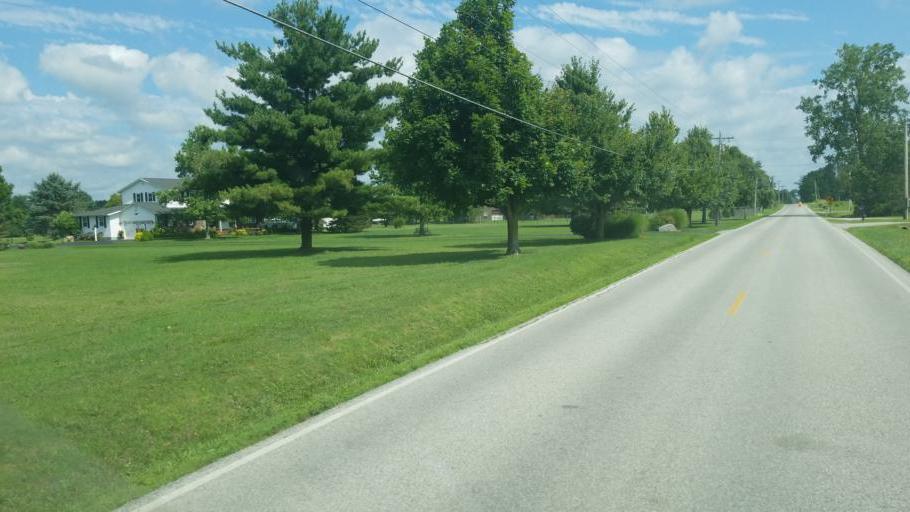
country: US
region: Ohio
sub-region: Delaware County
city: Sunbury
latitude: 40.2864
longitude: -82.9354
